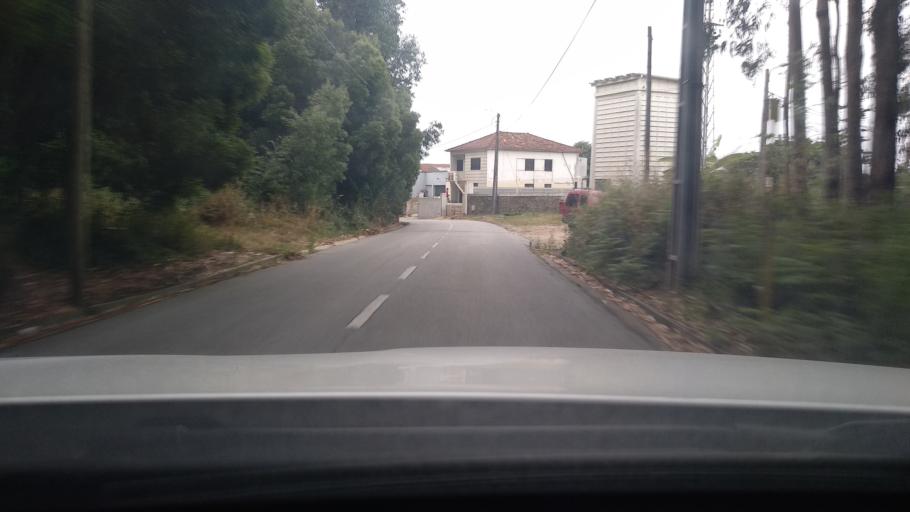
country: PT
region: Aveiro
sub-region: Espinho
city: Souto
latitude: 40.9838
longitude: -8.6245
